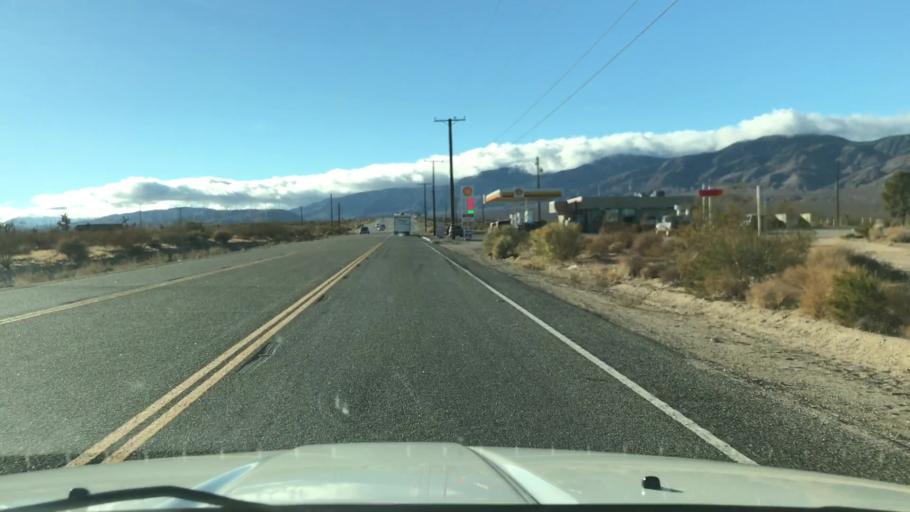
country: US
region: California
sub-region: Kern County
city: Mojave
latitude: 35.1255
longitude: -118.1163
